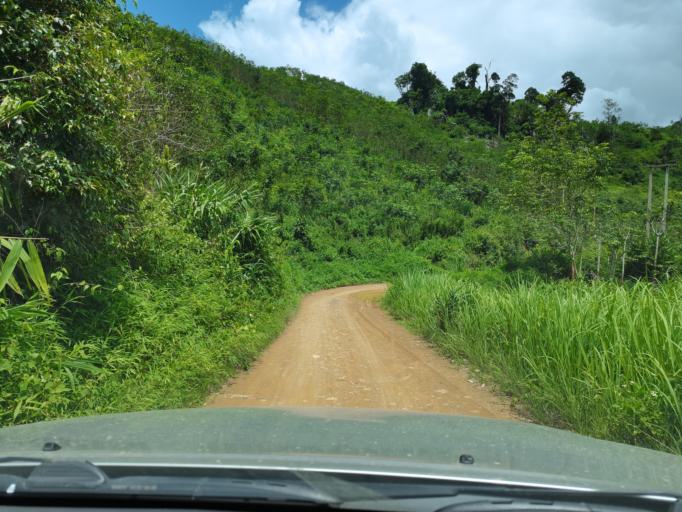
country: LA
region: Loungnamtha
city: Muang Long
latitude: 20.7180
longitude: 101.0141
